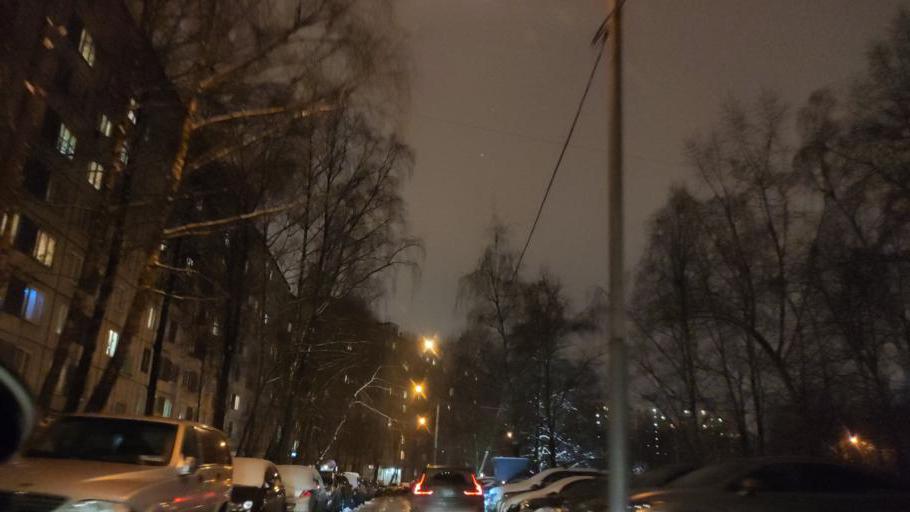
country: RU
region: Moscow
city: Tyoply Stan
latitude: 55.6165
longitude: 37.4954
